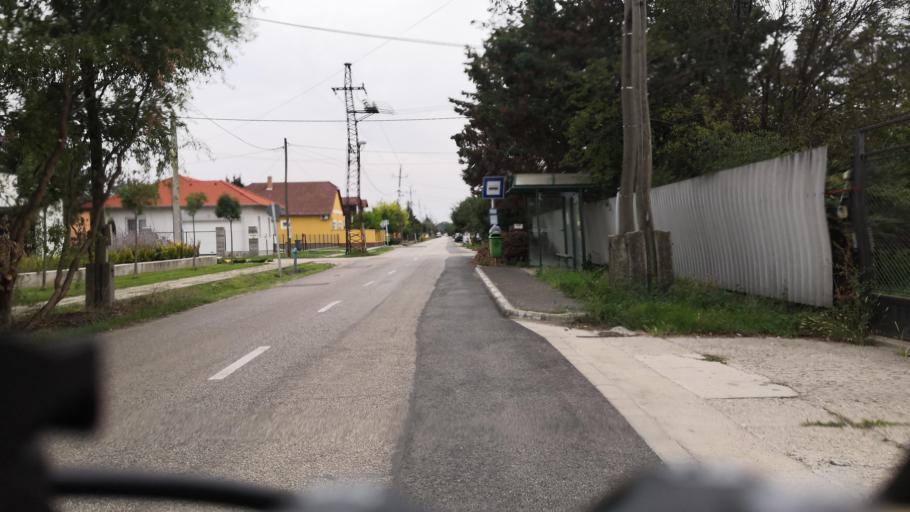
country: HU
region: Csongrad
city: Szeged
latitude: 46.2889
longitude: 20.1637
